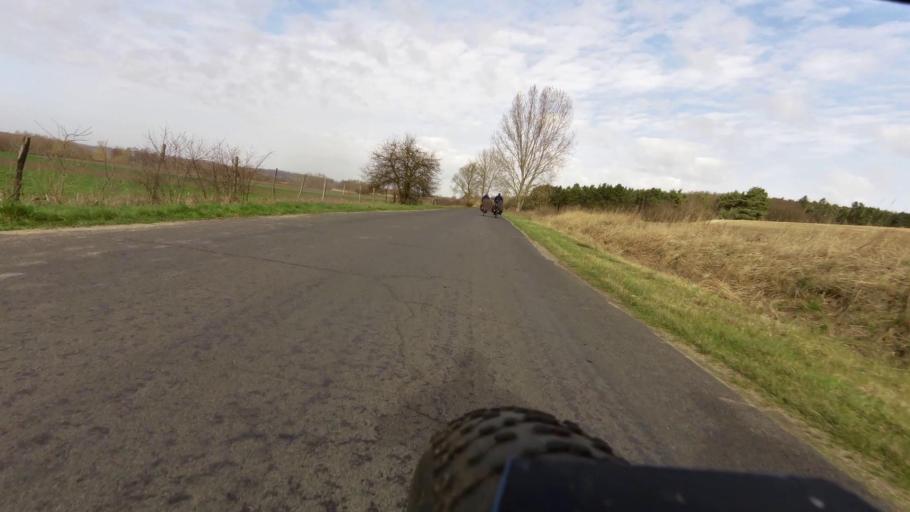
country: DE
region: Brandenburg
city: Brieskow-Finkenheerd
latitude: 52.2872
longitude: 14.6140
